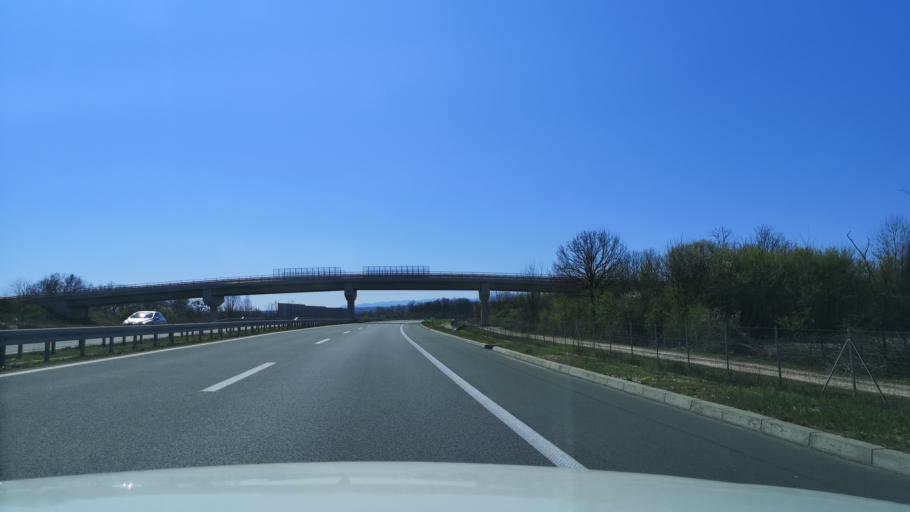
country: RS
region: Central Serbia
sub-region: Kolubarski Okrug
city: Lajkovac
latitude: 44.3798
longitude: 20.1152
